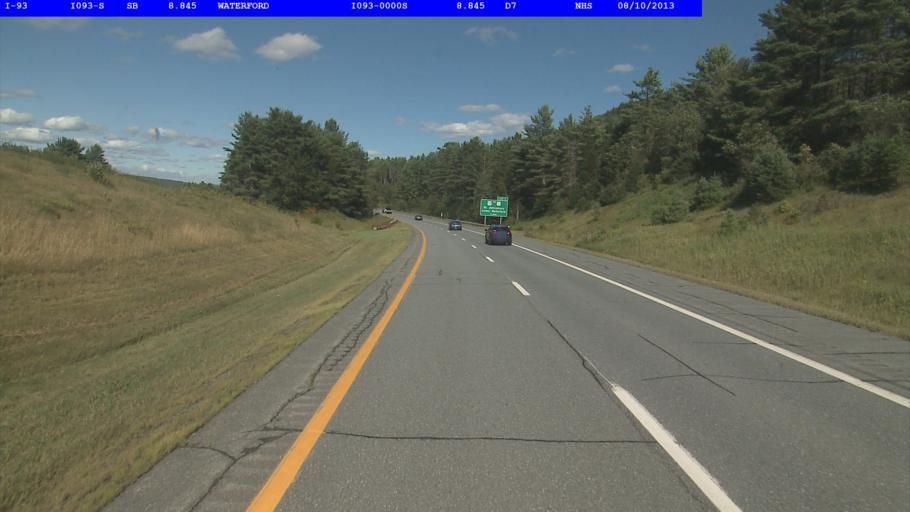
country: US
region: Vermont
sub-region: Caledonia County
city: Saint Johnsbury
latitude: 44.4162
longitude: -71.9791
